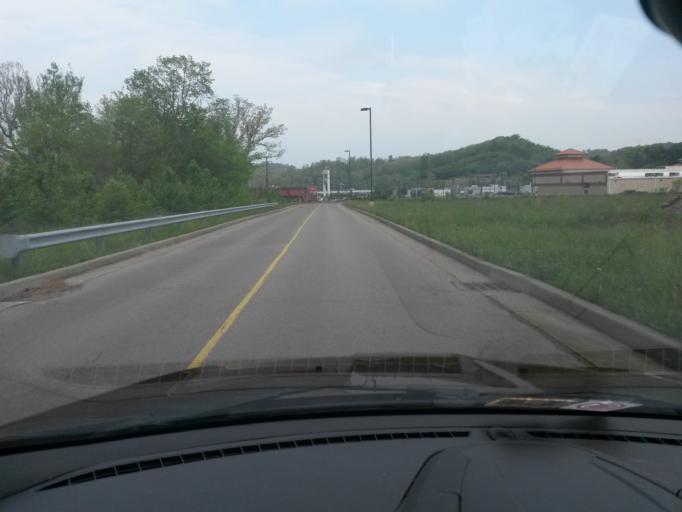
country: US
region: West Virginia
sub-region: Randolph County
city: Elkins
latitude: 38.8940
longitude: -79.8430
